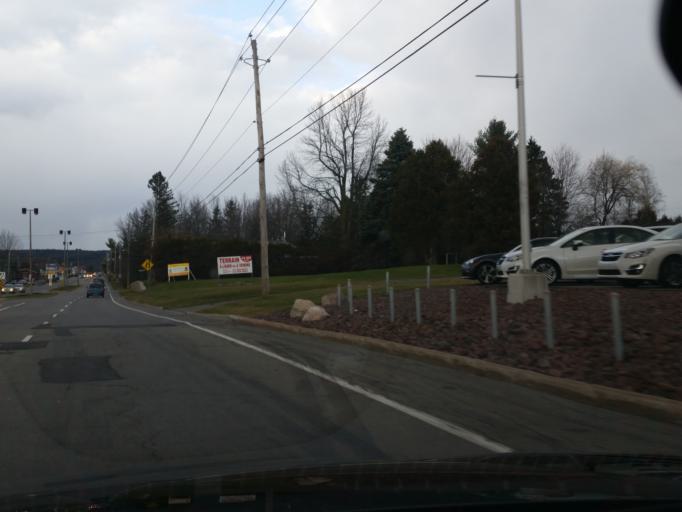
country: CA
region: Quebec
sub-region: Laurentides
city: Lachute
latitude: 45.6432
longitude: -74.3285
